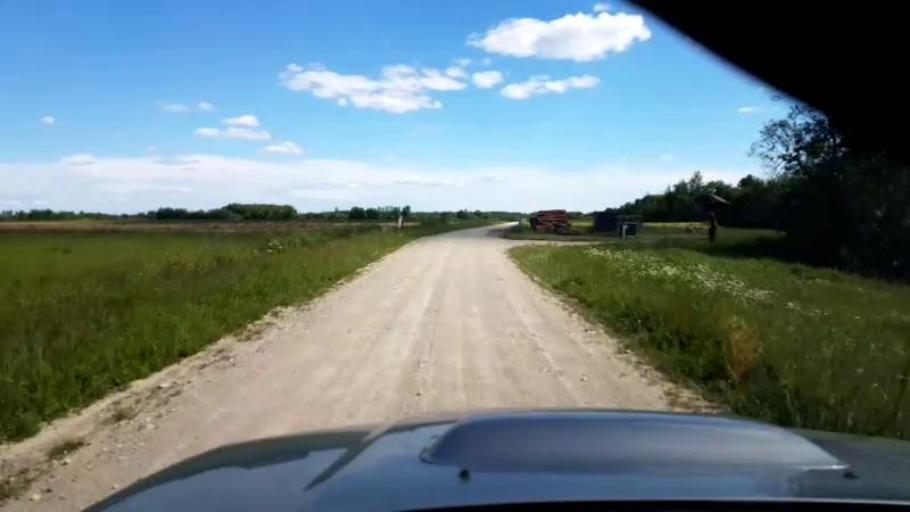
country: EE
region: Paernumaa
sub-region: Sauga vald
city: Sauga
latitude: 58.5038
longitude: 24.5225
